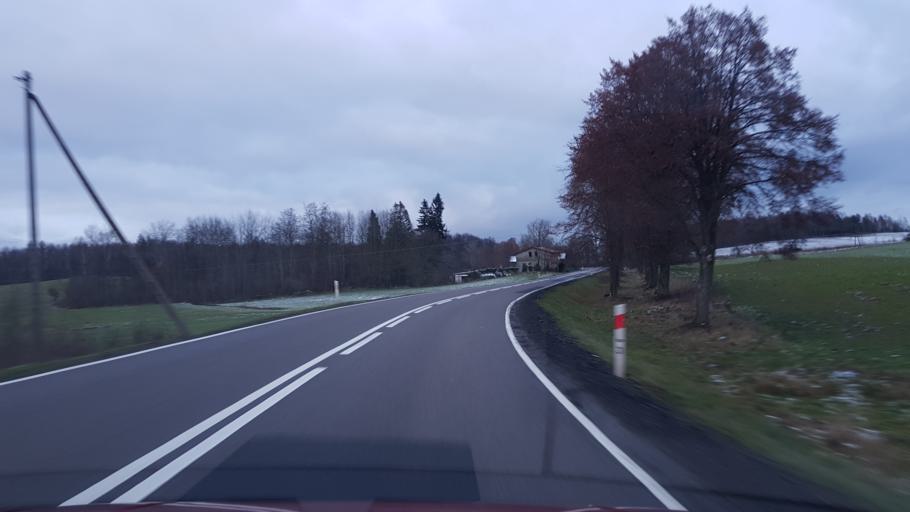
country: PL
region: Pomeranian Voivodeship
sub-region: Powiat bytowski
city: Tuchomie
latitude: 54.0843
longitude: 17.3005
